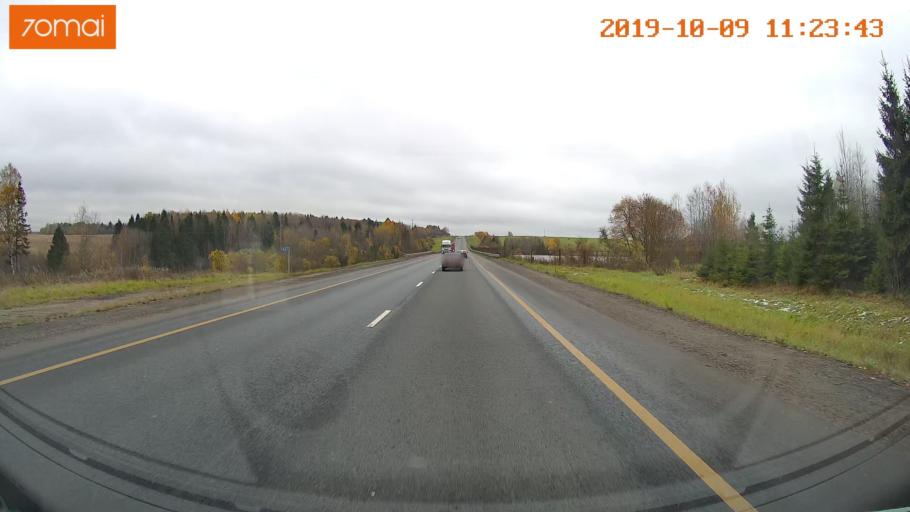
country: RU
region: Vologda
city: Vologda
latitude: 59.1182
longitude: 39.9727
